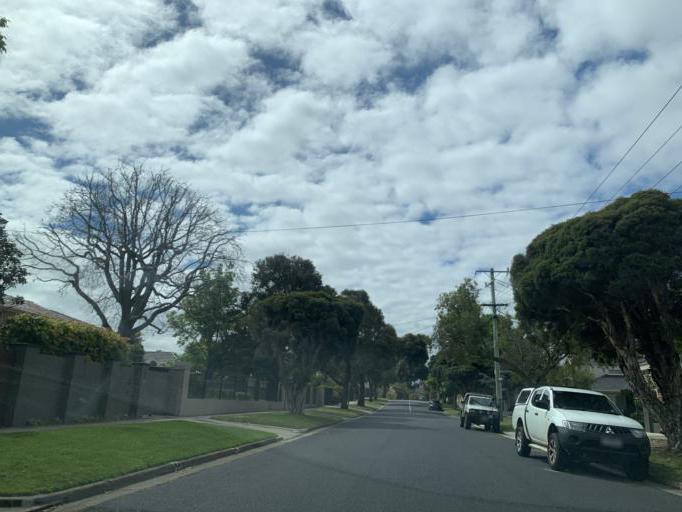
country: AU
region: Victoria
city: Beaumaris
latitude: -37.9875
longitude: 145.0445
